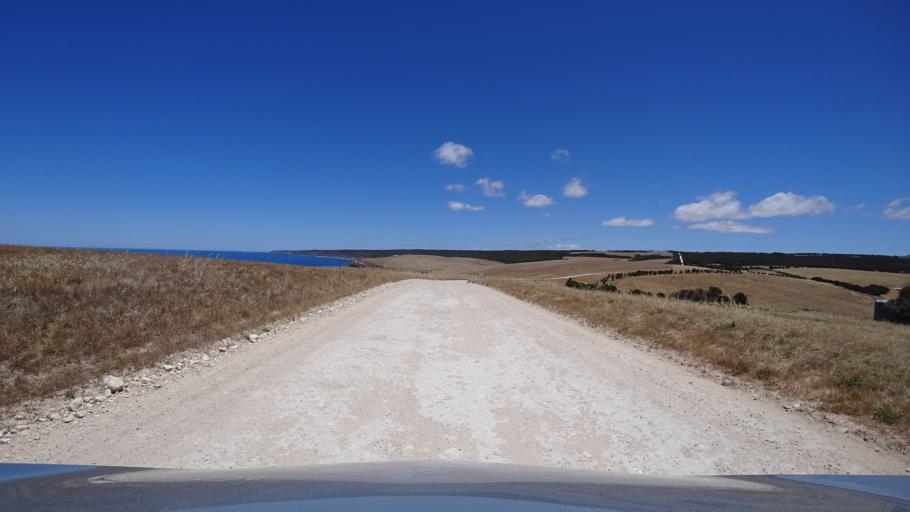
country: AU
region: South Australia
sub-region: Yankalilla
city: Normanville
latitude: -35.8427
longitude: 138.1307
